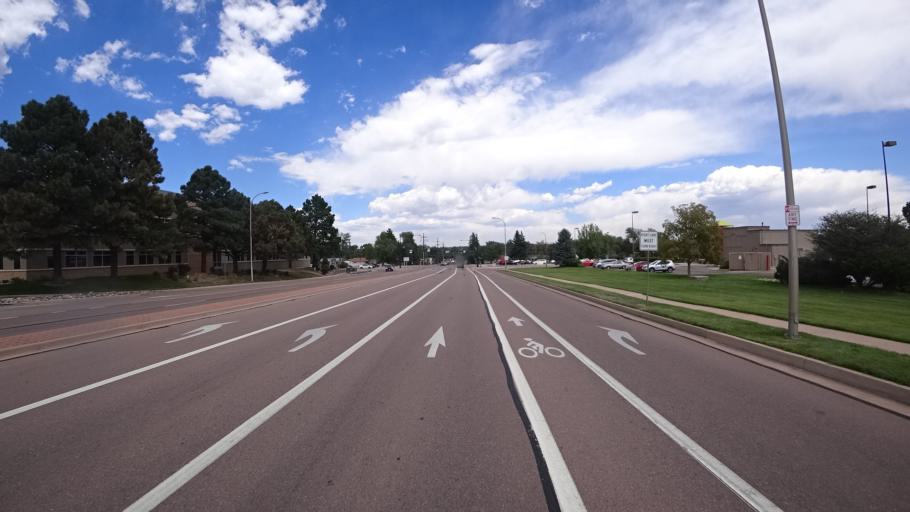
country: US
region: Colorado
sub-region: El Paso County
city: Stratmoor
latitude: 38.7945
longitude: -104.8034
